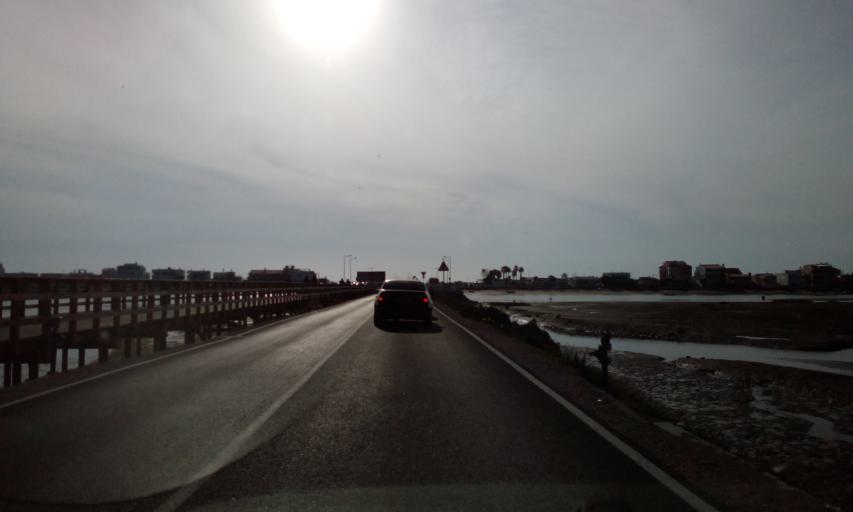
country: PT
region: Faro
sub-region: Faro
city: Faro
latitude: 37.0109
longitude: -7.9917
